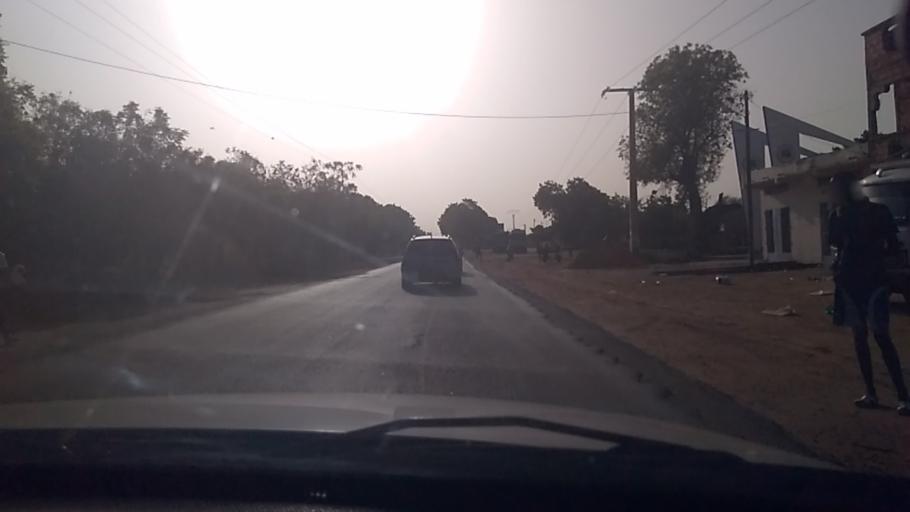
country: SN
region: Thies
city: Khombole
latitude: 14.7638
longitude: -16.7981
